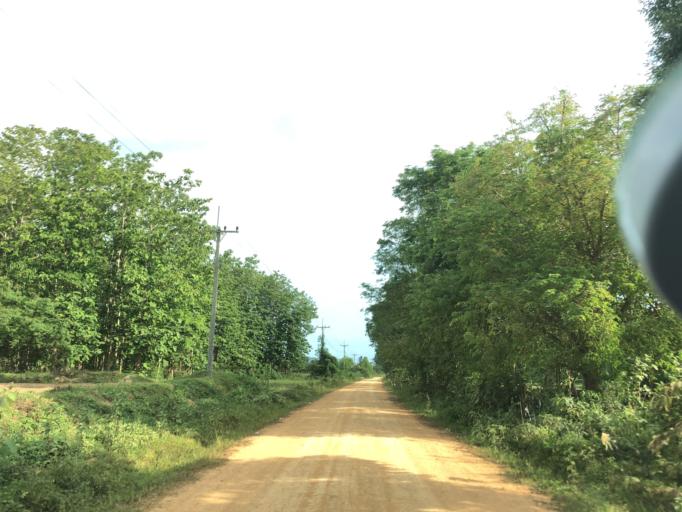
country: TH
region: Loei
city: Chiang Khan
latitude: 18.0024
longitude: 101.4201
